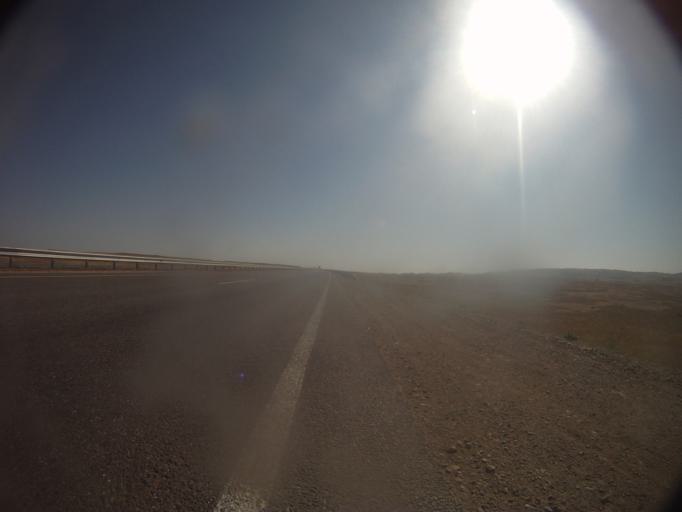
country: KZ
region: Zhambyl
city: Taraz
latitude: 42.7393
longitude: 70.9277
